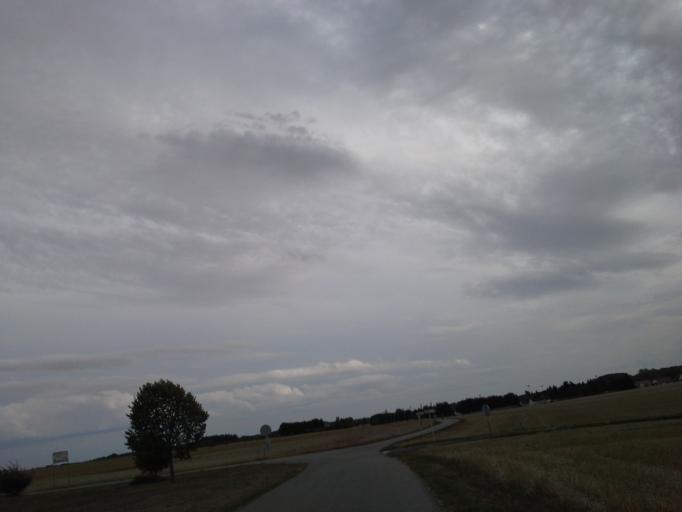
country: FR
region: Centre
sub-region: Departement du Loir-et-Cher
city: Villiers-sur-Loir
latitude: 47.8001
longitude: 0.9988
